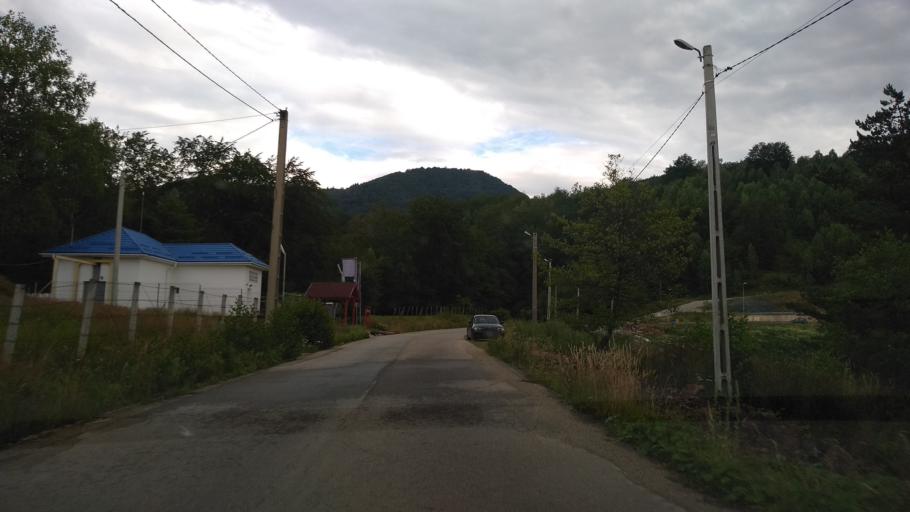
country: RO
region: Hunedoara
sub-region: Municipiul  Vulcan
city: Jiu-Paroseni
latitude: 45.3555
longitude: 23.2901
